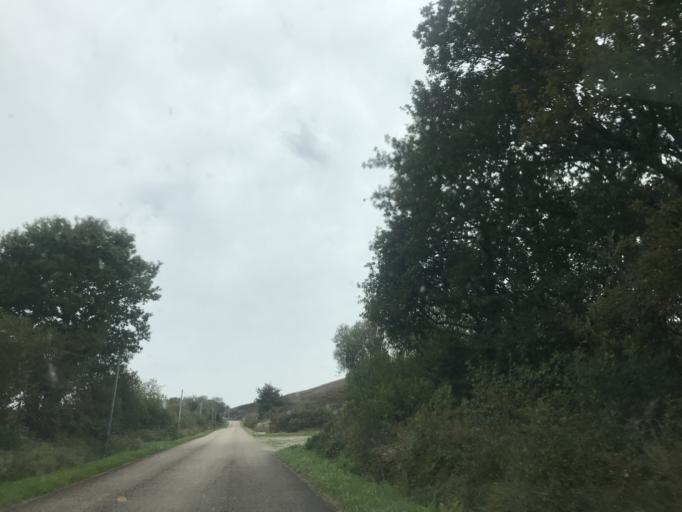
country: FR
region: Brittany
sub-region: Departement du Finistere
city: Brasparts
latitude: 48.3830
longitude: -3.9362
